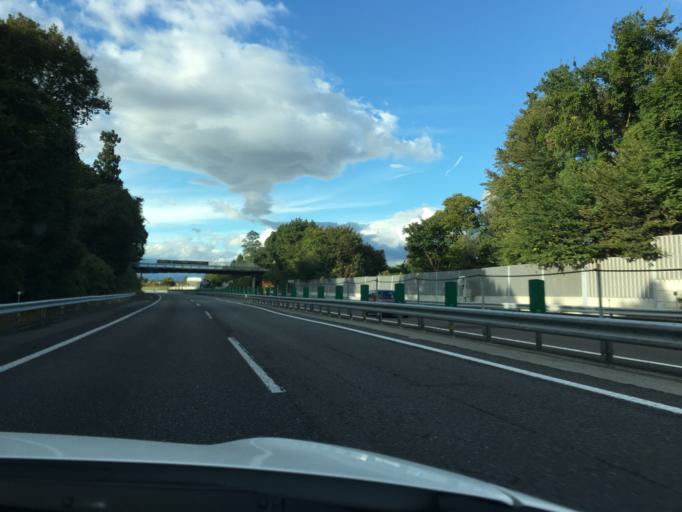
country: JP
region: Fukushima
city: Sukagawa
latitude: 37.3382
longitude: 140.3360
